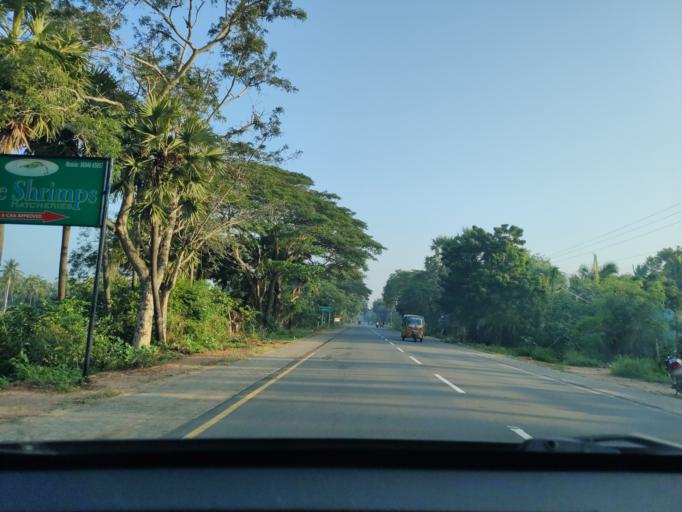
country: IN
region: Tamil Nadu
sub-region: Villupuram
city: Auroville
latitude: 12.0643
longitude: 79.8780
